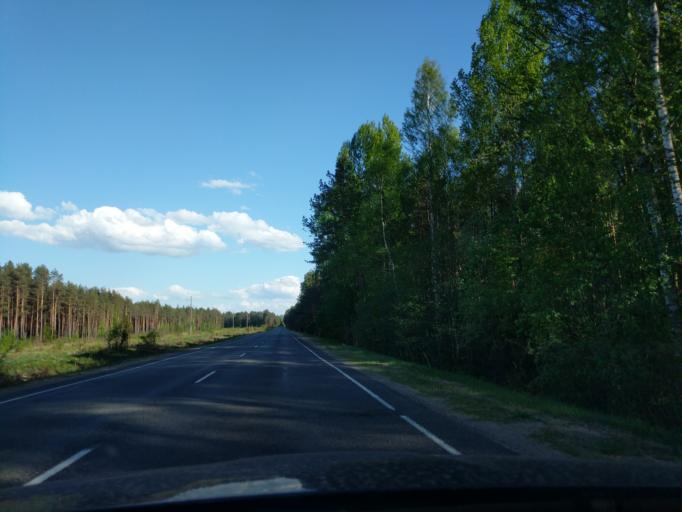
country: BY
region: Minsk
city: Kryvichy
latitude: 54.7477
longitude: 27.1178
